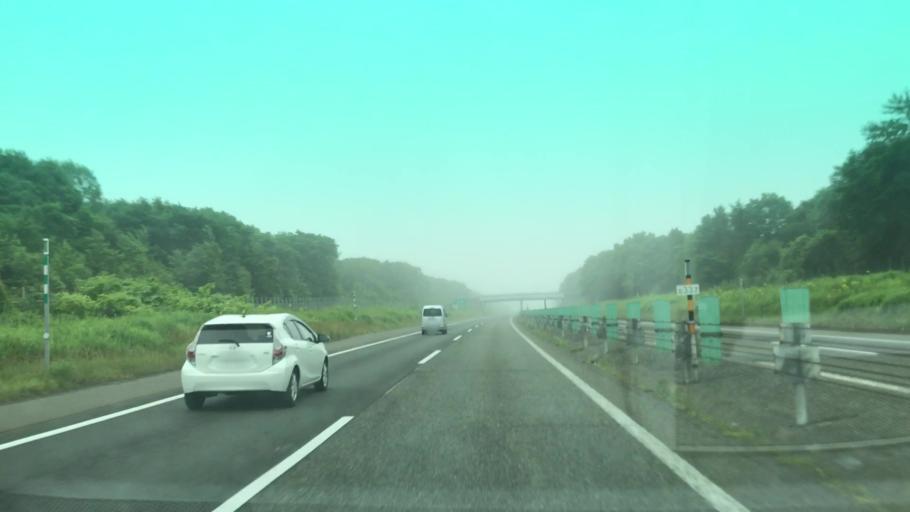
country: JP
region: Hokkaido
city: Chitose
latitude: 42.8259
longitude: 141.6150
